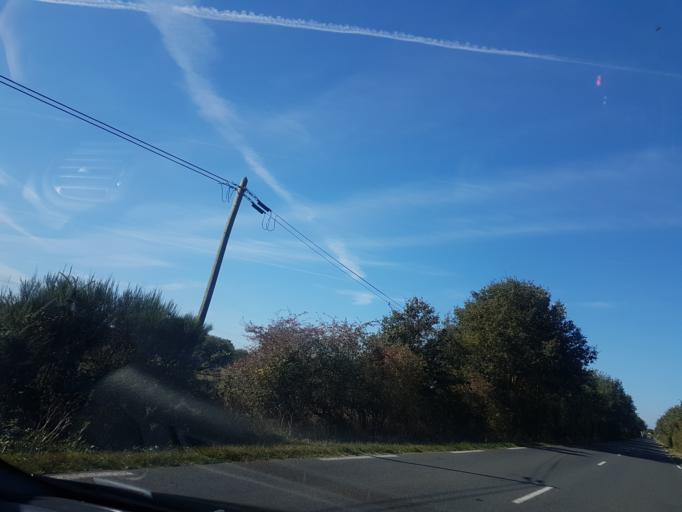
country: FR
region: Pays de la Loire
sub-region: Departement de la Loire-Atlantique
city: Casson
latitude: 47.4278
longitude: -1.5942
